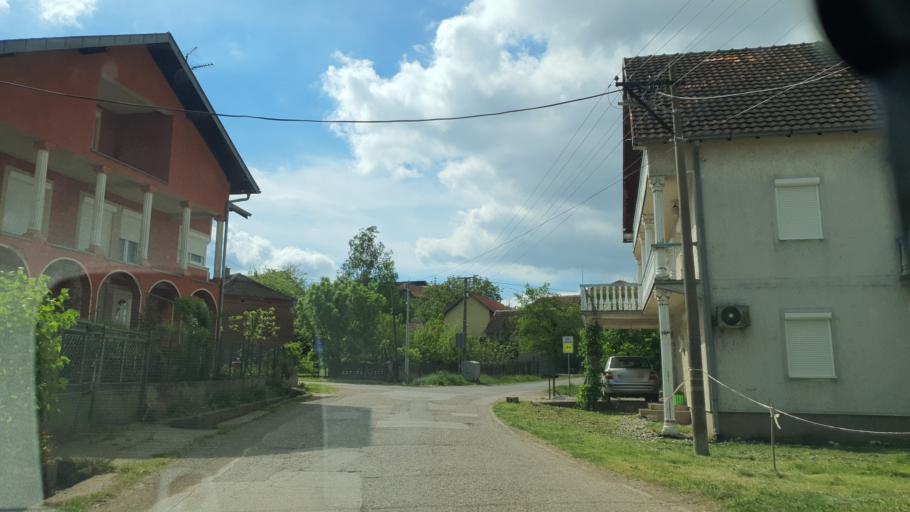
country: RS
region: Central Serbia
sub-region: Pomoravski Okrug
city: Paracin
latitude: 43.9425
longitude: 21.4944
